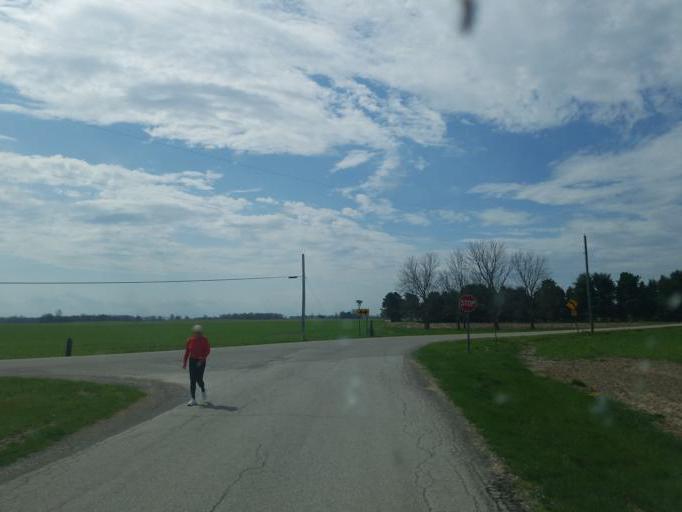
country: US
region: Ohio
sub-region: Crawford County
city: Bucyrus
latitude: 40.7790
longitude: -83.0266
